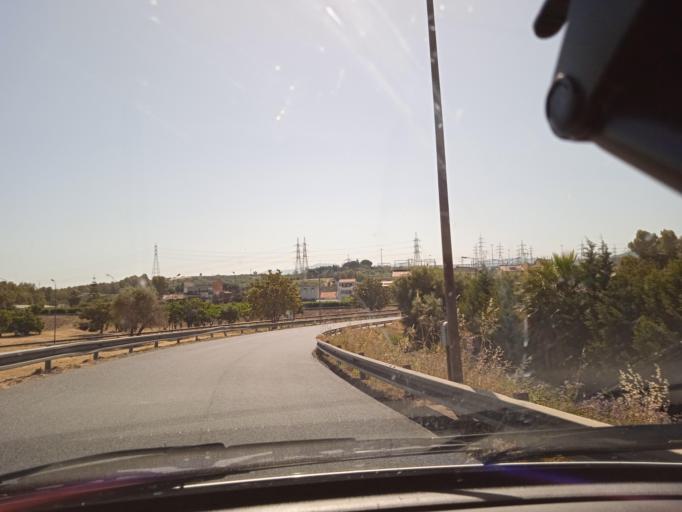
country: IT
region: Sicily
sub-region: Messina
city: San Filippo del Mela
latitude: 38.1915
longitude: 15.2732
